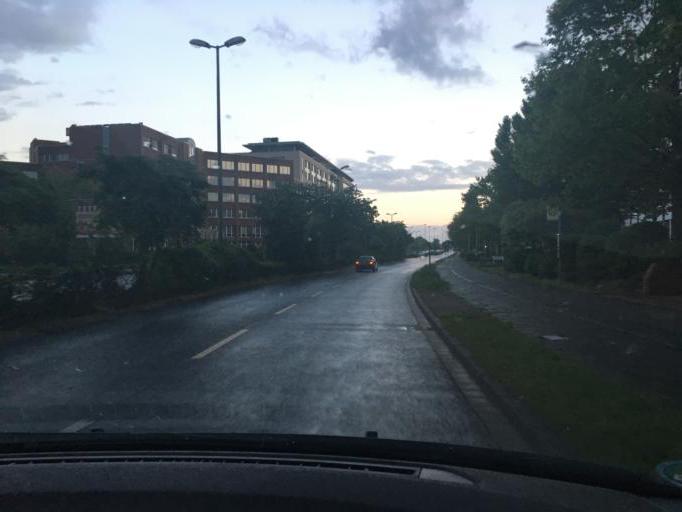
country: DE
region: North Rhine-Westphalia
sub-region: Regierungsbezirk Dusseldorf
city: Neuss
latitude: 51.1952
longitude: 6.7112
